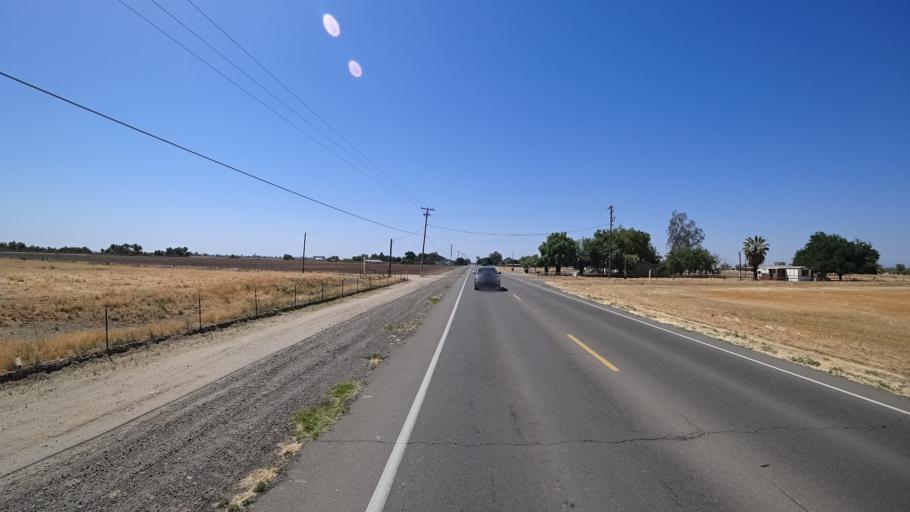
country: US
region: California
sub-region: Kings County
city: Lemoore
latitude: 36.2623
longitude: -119.7809
